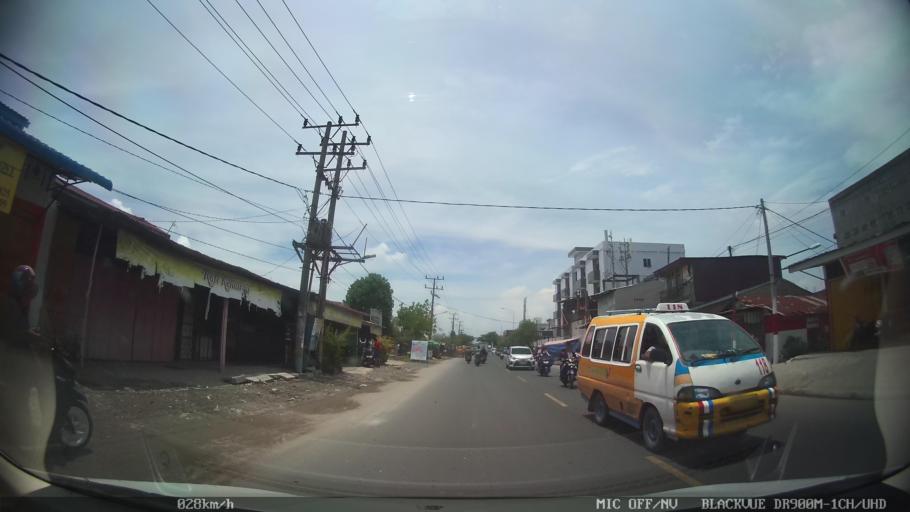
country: ID
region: North Sumatra
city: Belawan
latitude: 3.7747
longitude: 98.6812
